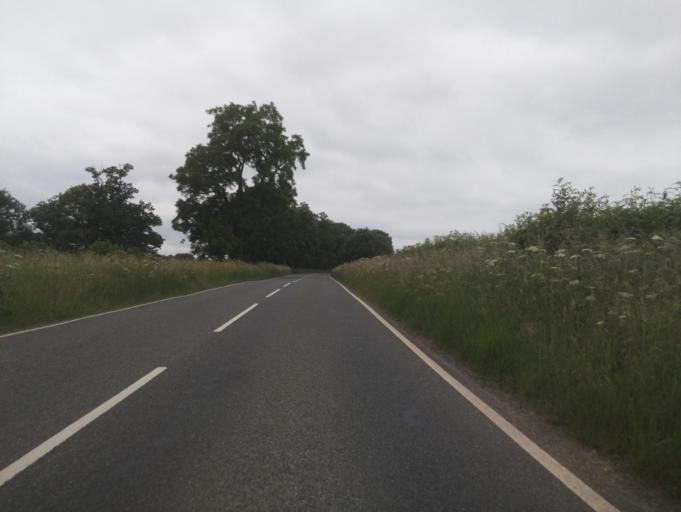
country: GB
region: England
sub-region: District of Rutland
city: Wing
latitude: 52.6359
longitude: -0.6654
